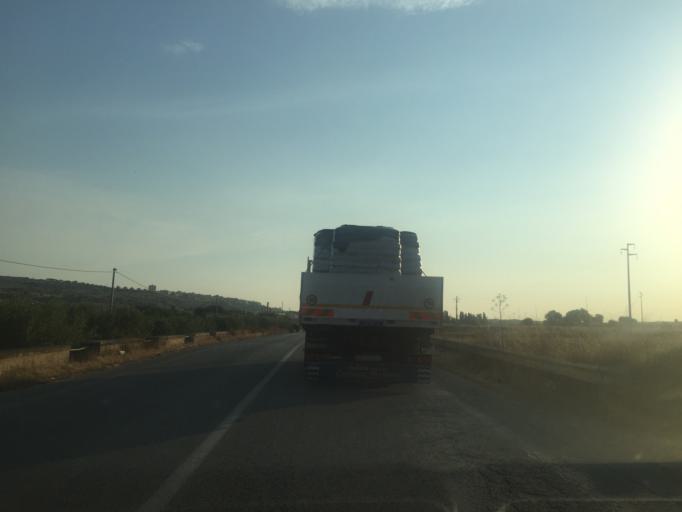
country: IT
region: Sicily
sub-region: Ragusa
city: Ispica
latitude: 36.7644
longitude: 14.8993
